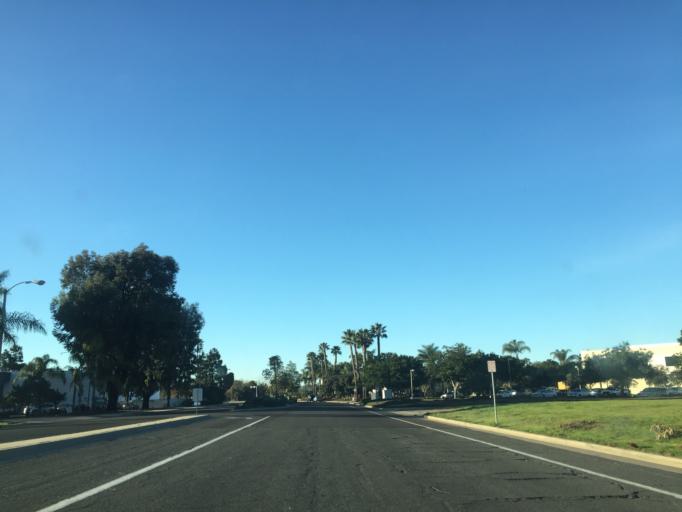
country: US
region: California
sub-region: Santa Barbara County
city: Isla Vista
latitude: 34.4330
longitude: -119.8537
